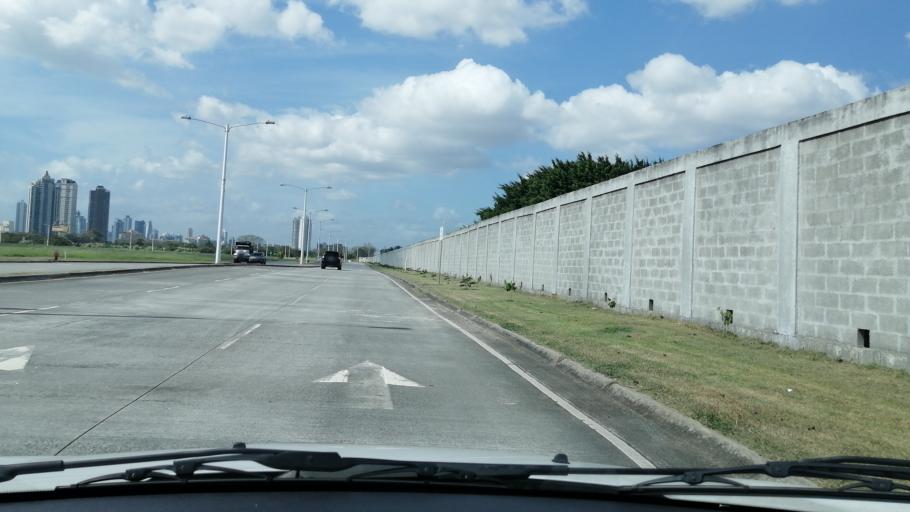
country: PA
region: Panama
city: San Miguelito
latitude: 9.0358
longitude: -79.4429
